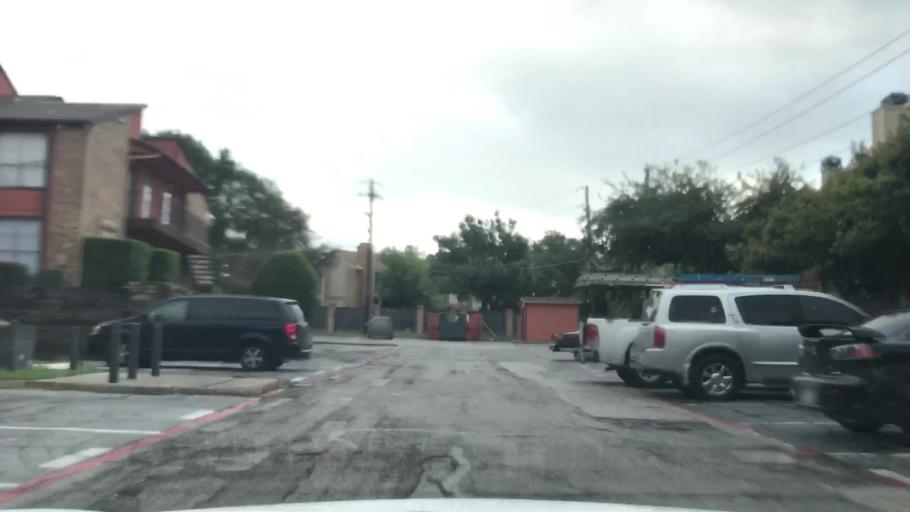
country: US
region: Texas
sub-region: Dallas County
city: Richardson
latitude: 32.8973
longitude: -96.7272
